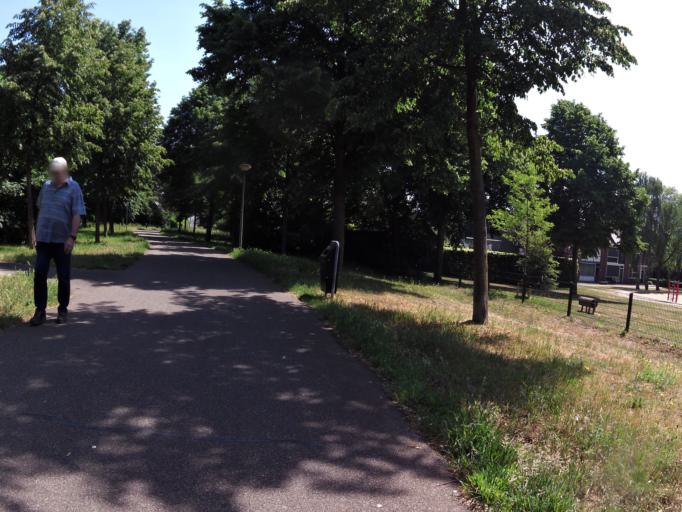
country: NL
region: North Brabant
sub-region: Gemeente 's-Hertogenbosch
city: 's-Hertogenbosch
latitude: 51.7056
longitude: 5.3157
